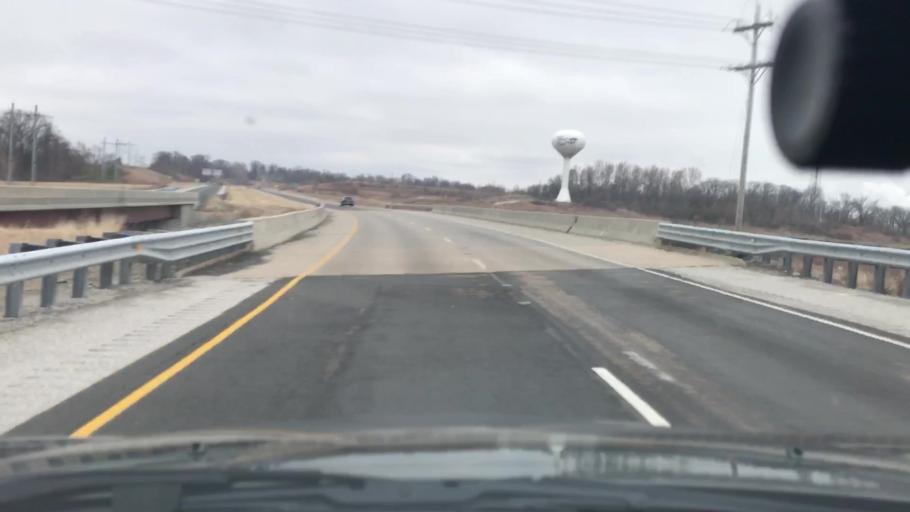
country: US
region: Illinois
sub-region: Madison County
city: Roxana
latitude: 38.8714
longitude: -90.0604
